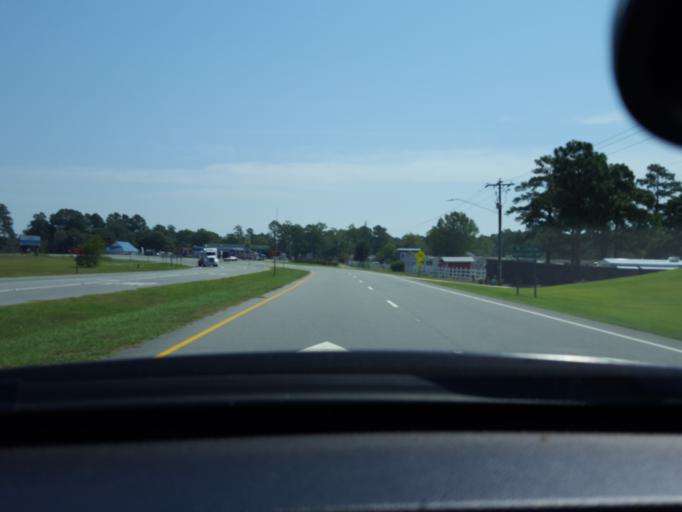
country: US
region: North Carolina
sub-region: Bladen County
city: Elizabethtown
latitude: 34.6553
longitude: -78.4974
